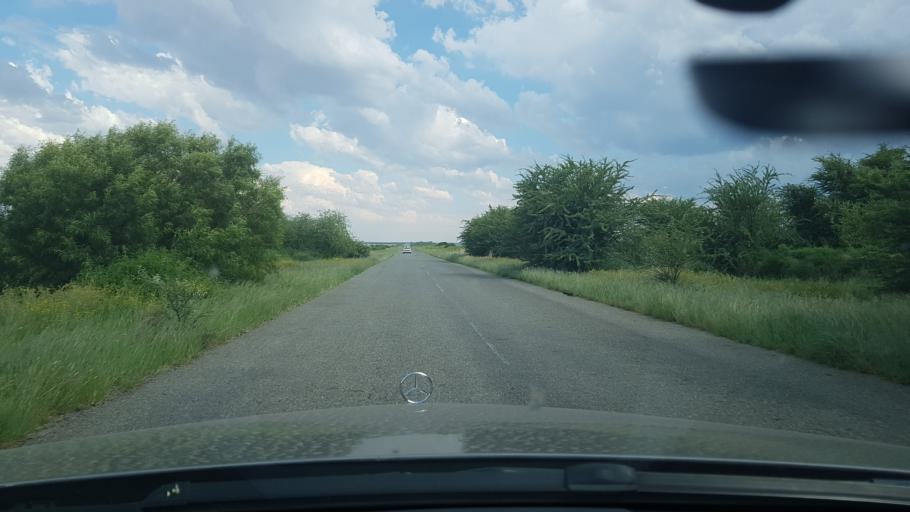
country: ZA
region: North-West
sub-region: Dr Ruth Segomotsi Mompati District Municipality
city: Bloemhof
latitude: -27.8314
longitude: 25.6368
